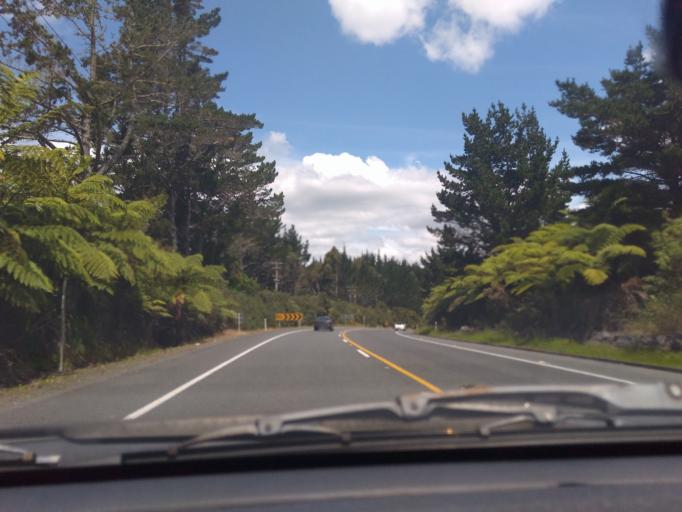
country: NZ
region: Northland
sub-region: Far North District
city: Kerikeri
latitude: -35.2812
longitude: 173.9555
